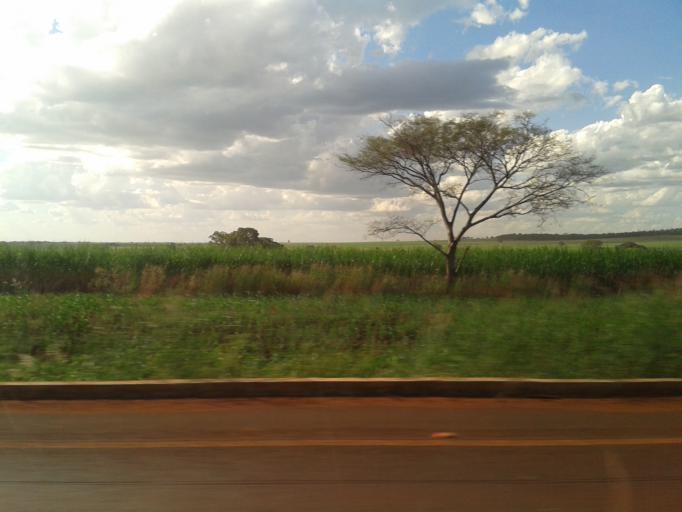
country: BR
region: Minas Gerais
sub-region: Santa Vitoria
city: Santa Vitoria
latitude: -18.6943
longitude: -49.9228
